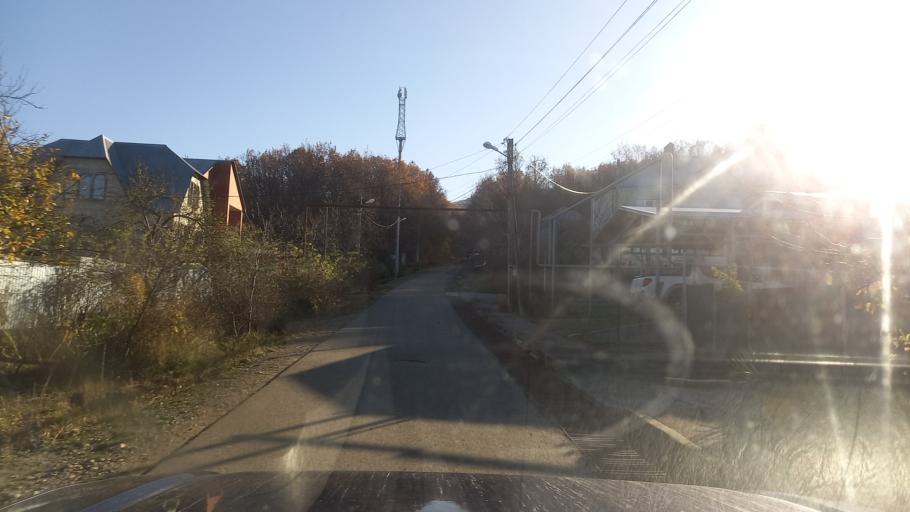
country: RU
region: Krasnodarskiy
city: Goryachiy Klyuch
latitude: 44.6189
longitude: 39.1044
